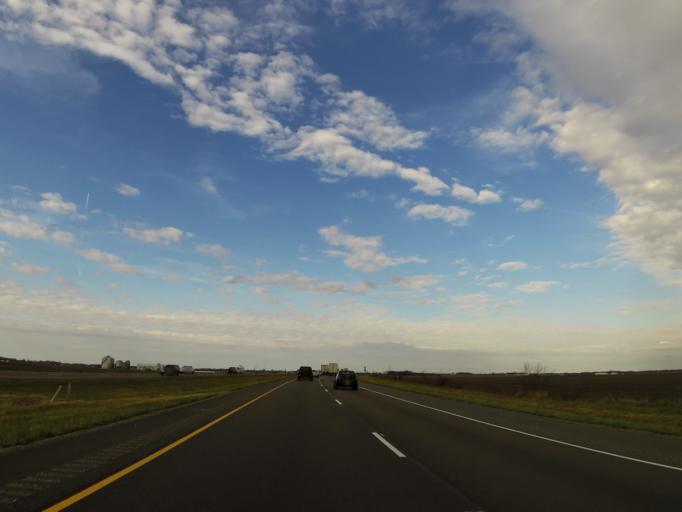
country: US
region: Illinois
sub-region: Washington County
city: Okawville
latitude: 38.4283
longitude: -89.4872
